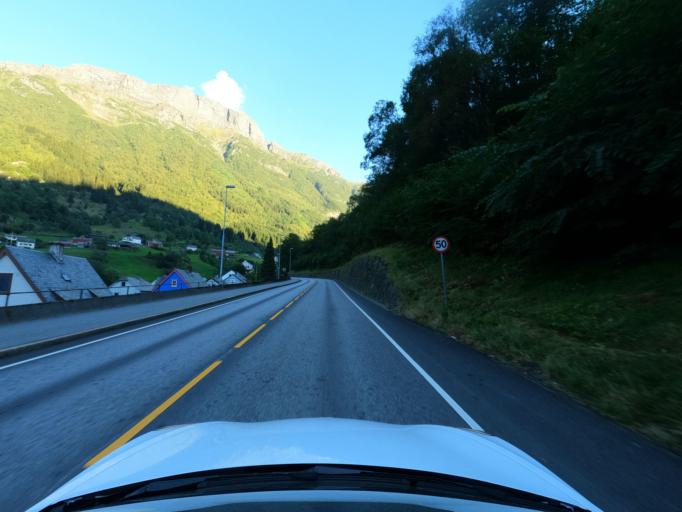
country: NO
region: Hordaland
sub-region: Odda
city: Odda
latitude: 60.0570
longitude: 6.5500
